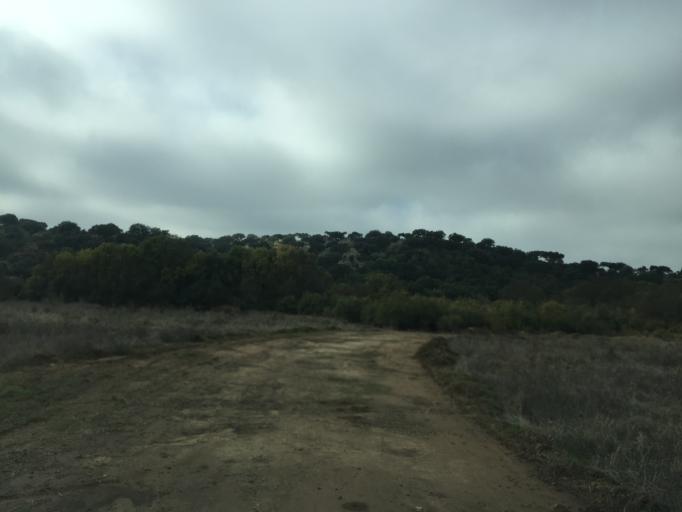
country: PT
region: Portalegre
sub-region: Fronteira
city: Fronteira
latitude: 39.0676
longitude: -7.6177
